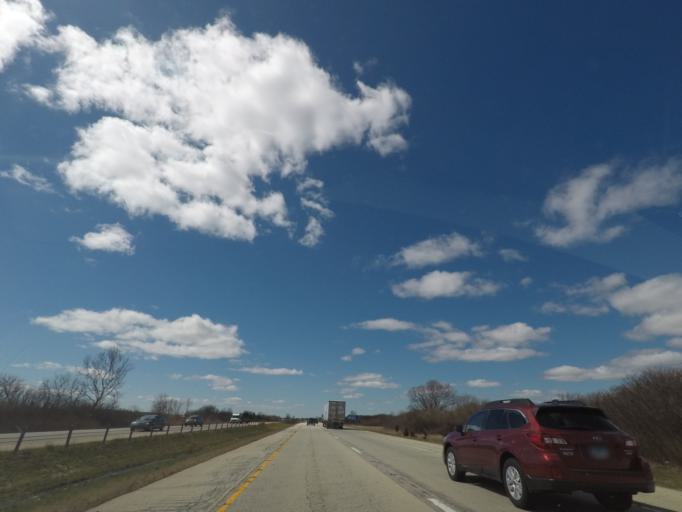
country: US
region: Illinois
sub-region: Grundy County
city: Gardner
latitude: 41.2036
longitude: -88.3055
